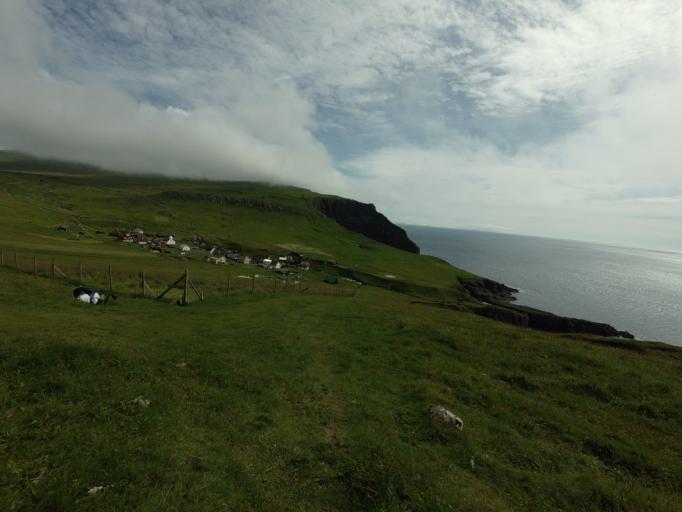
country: FO
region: Vagar
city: Sorvagur
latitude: 62.1039
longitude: -7.6504
